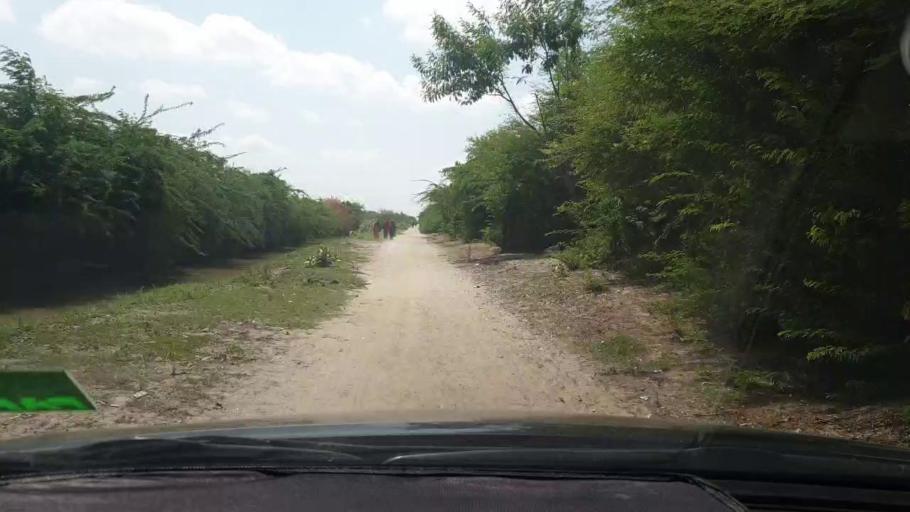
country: PK
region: Sindh
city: Tando Bago
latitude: 24.8741
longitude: 69.0709
